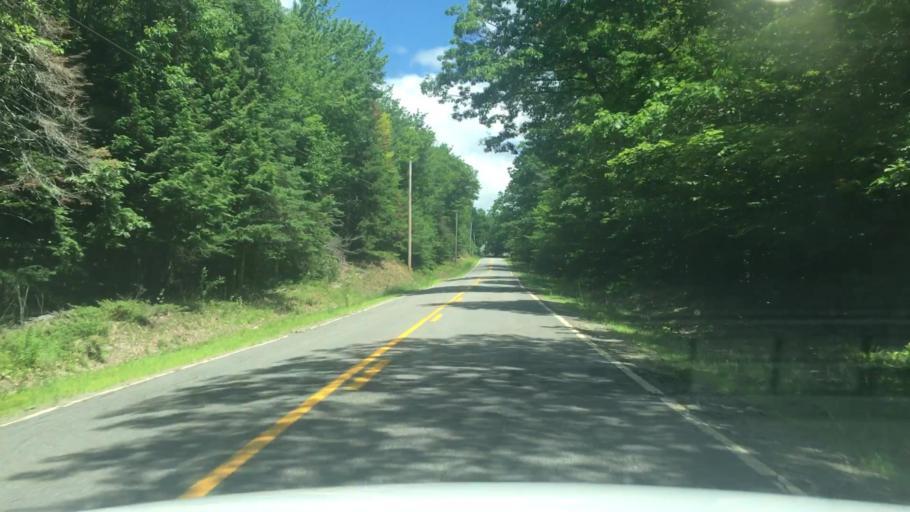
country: US
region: Maine
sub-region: Waldo County
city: Searsmont
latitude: 44.4444
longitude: -69.3065
